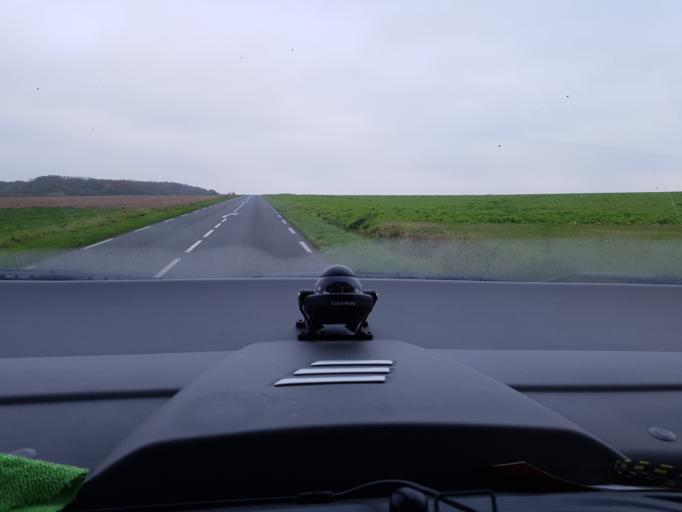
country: FR
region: Picardie
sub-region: Departement de la Somme
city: Ault
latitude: 50.1117
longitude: 1.4777
